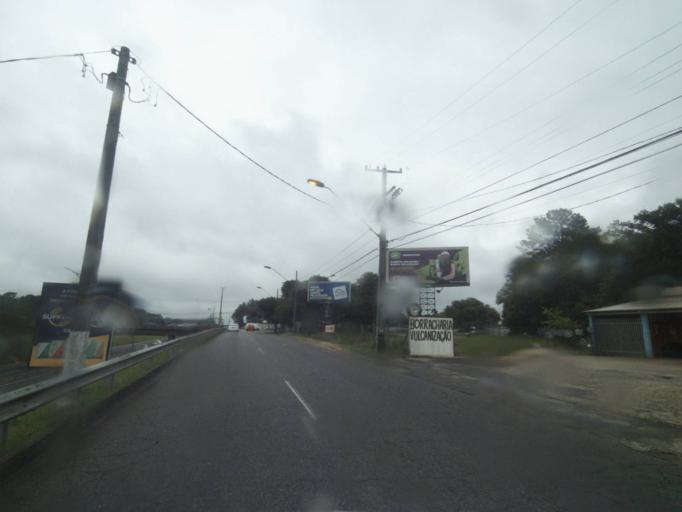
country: BR
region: Parana
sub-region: Curitiba
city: Curitiba
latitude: -25.4302
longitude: -49.3523
